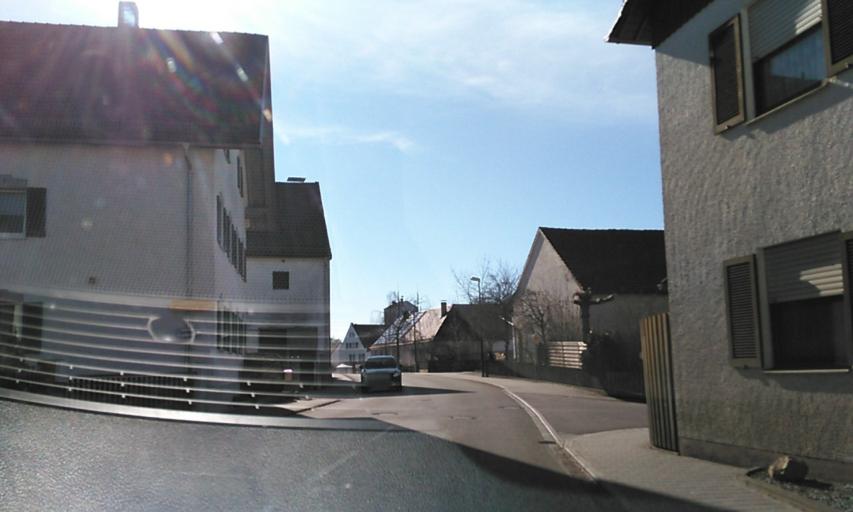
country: DE
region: Bavaria
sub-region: Swabia
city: Merching
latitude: 48.2454
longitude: 10.9852
